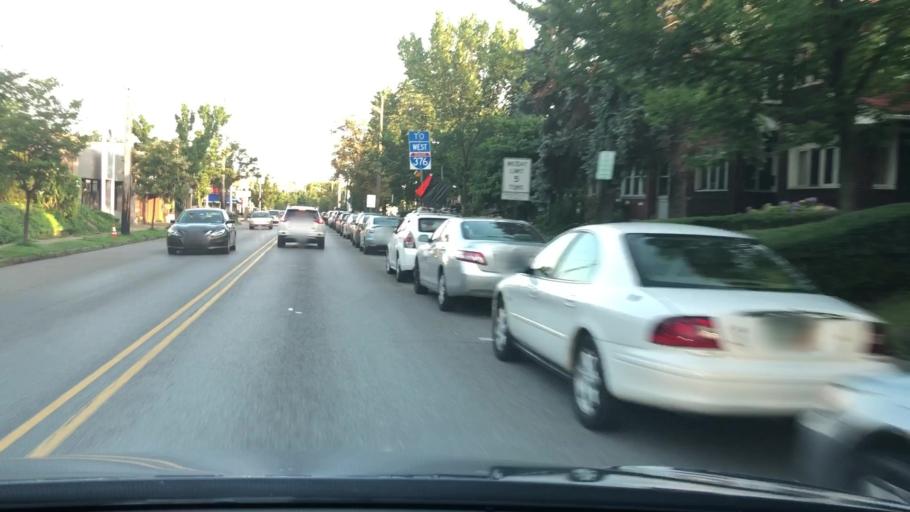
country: US
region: Pennsylvania
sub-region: Allegheny County
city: Edgewood
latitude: 40.4339
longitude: -79.8948
